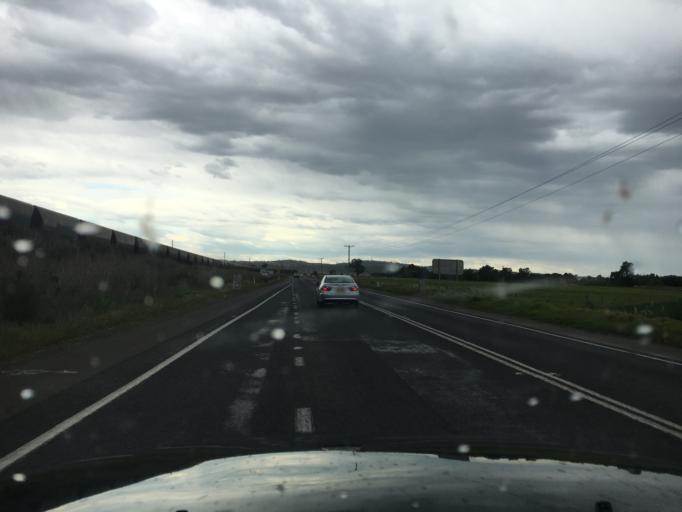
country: AU
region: New South Wales
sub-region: Muswellbrook
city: Muswellbrook
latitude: -32.2112
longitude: 150.8962
